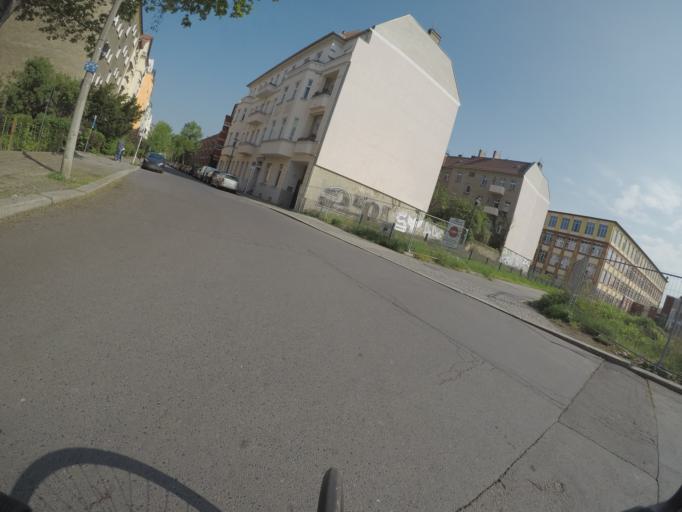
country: DE
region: Berlin
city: Pankow
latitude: 52.5706
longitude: 13.4165
